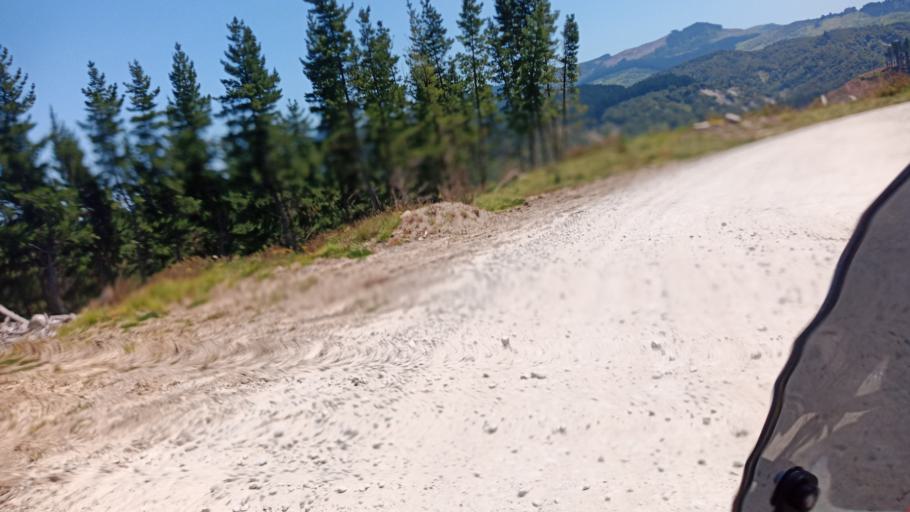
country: NZ
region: Gisborne
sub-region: Gisborne District
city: Gisborne
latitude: -38.2914
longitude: 178.0066
